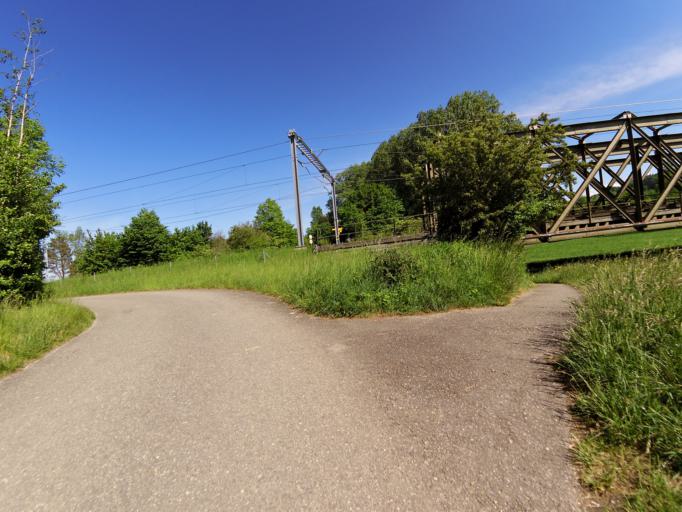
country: CH
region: Thurgau
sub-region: Frauenfeld District
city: Mullheim
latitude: 47.5856
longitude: 9.0072
